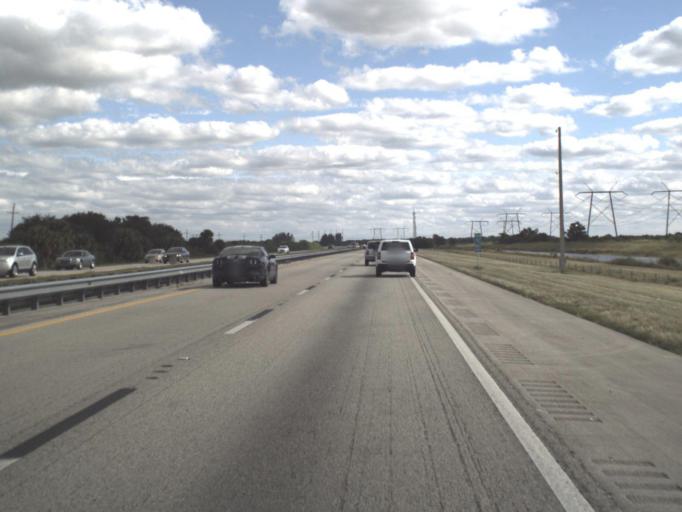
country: US
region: Florida
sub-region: Indian River County
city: West Vero Corridor
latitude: 27.4983
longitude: -80.5788
